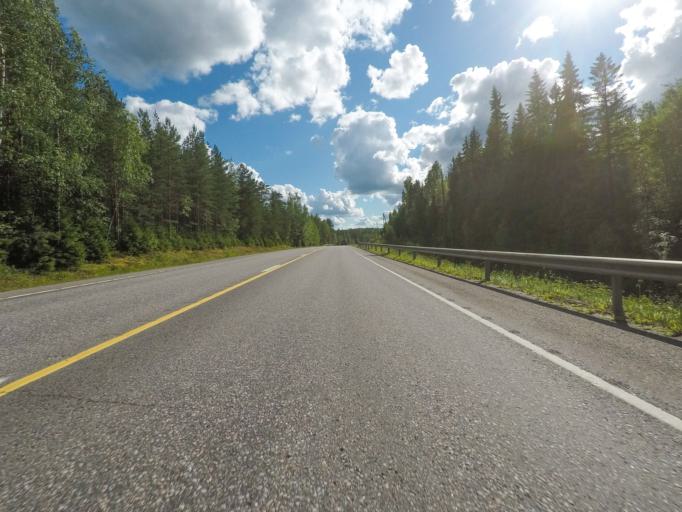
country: FI
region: Uusimaa
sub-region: Helsinki
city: Nurmijaervi
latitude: 60.5251
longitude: 24.6679
